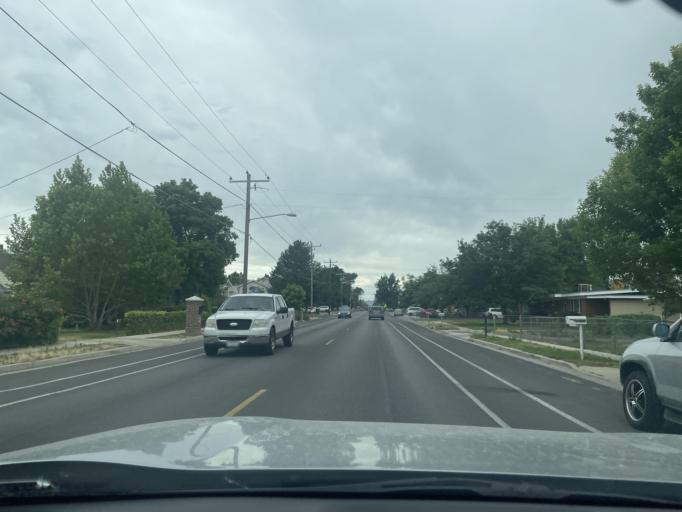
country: US
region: Utah
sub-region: Salt Lake County
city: Millcreek
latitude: 40.6938
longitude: -111.8770
